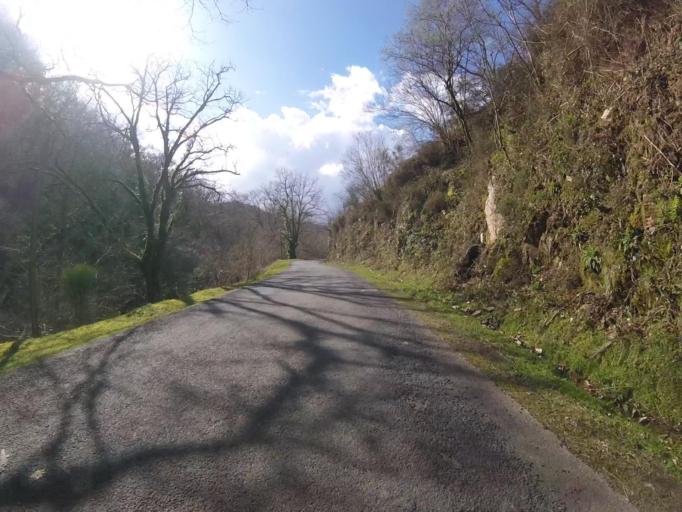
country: ES
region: Navarre
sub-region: Provincia de Navarra
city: Etxalar
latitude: 43.2645
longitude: -1.6049
